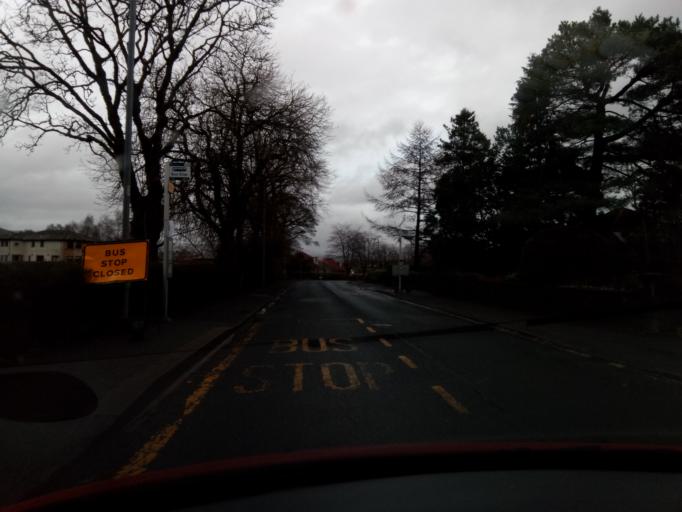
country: GB
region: Scotland
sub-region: East Dunbartonshire
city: Kirkintilloch
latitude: 55.9261
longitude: -4.1562
